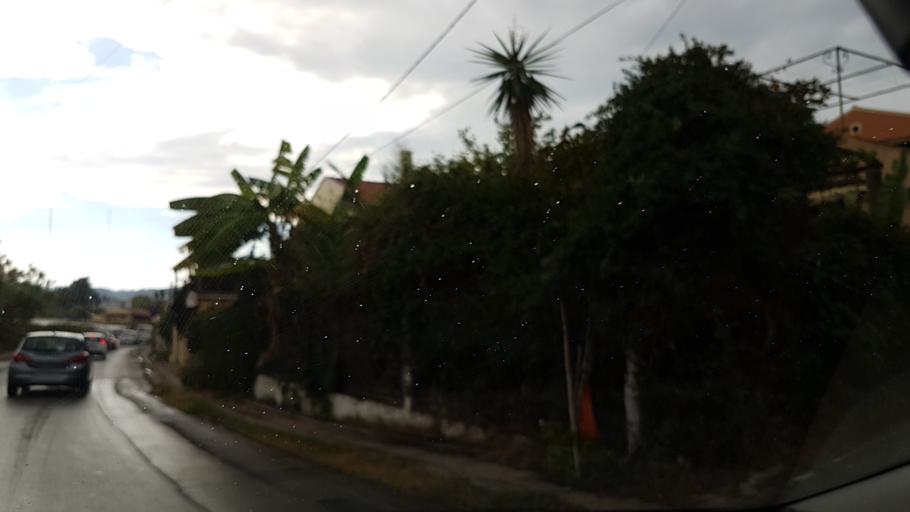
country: GR
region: Ionian Islands
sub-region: Nomos Kerkyras
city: Kerkyra
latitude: 39.6135
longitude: 19.9114
